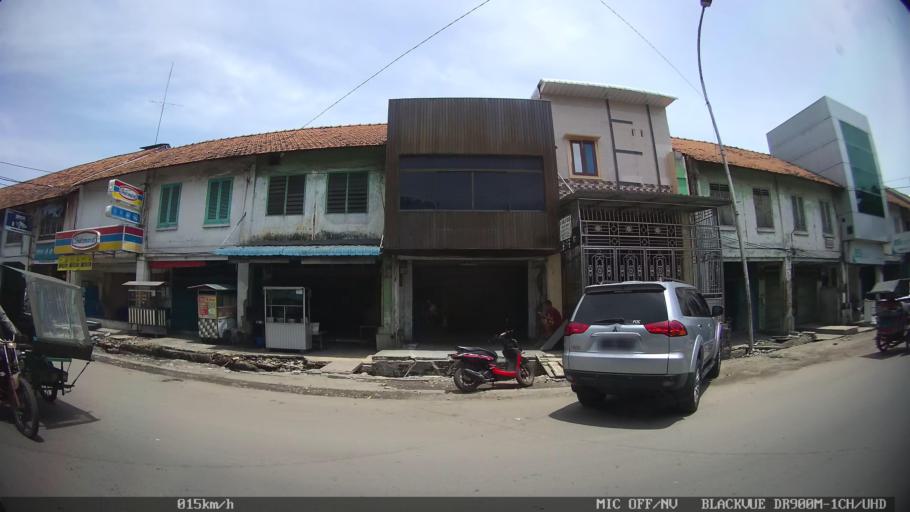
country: ID
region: North Sumatra
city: Belawan
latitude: 3.7828
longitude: 98.6850
